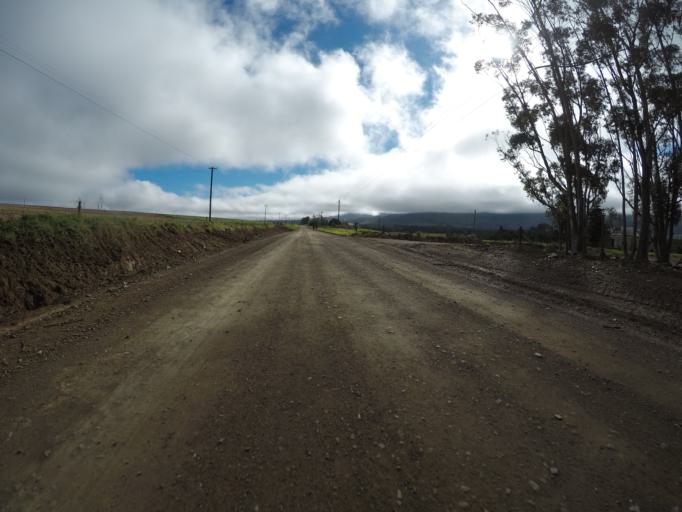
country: ZA
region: Western Cape
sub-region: Cape Winelands District Municipality
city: Ashton
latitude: -34.1338
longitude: 19.8565
